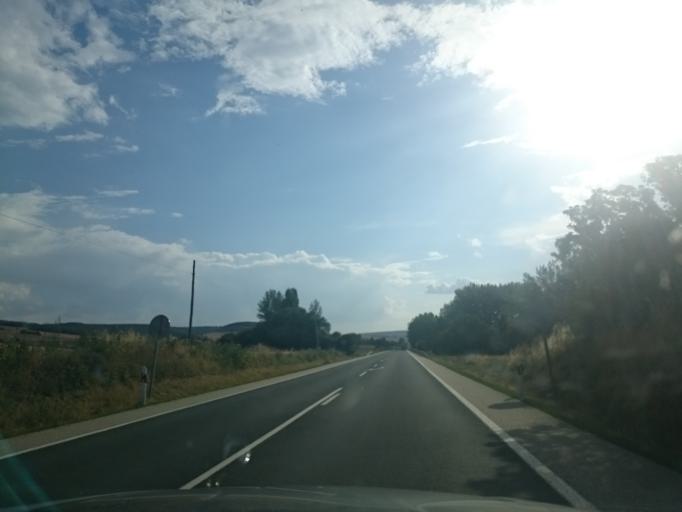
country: ES
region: Castille and Leon
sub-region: Provincia de Burgos
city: Tosantos
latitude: 42.4119
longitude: -3.2501
